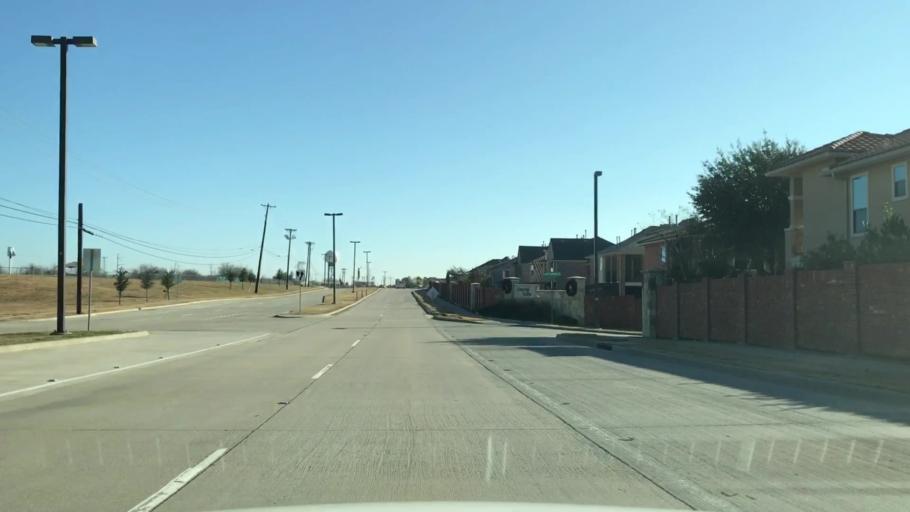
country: US
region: Texas
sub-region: Dallas County
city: Coppell
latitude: 32.9255
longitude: -96.9760
